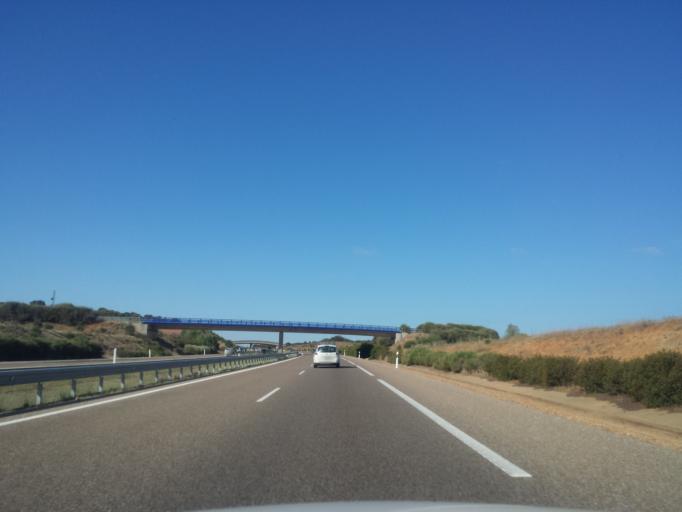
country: ES
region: Castille and Leon
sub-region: Provincia de Leon
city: Villamandos
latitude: 42.1873
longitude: -5.6195
